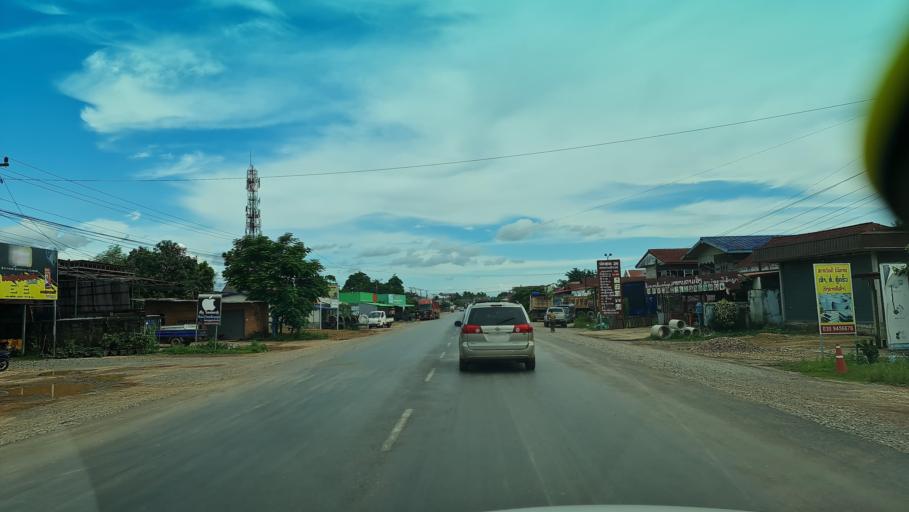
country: TH
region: Nakhon Phanom
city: Ban Phaeng
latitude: 18.1029
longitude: 104.2839
